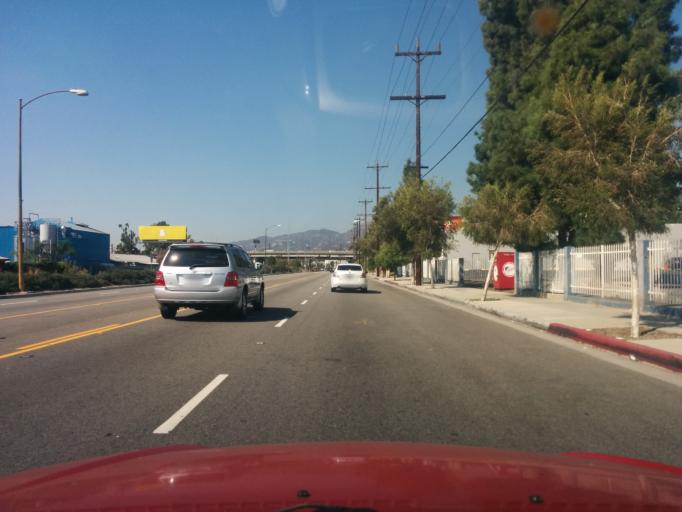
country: US
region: California
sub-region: Los Angeles County
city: North Glendale
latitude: 34.1509
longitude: -118.2739
